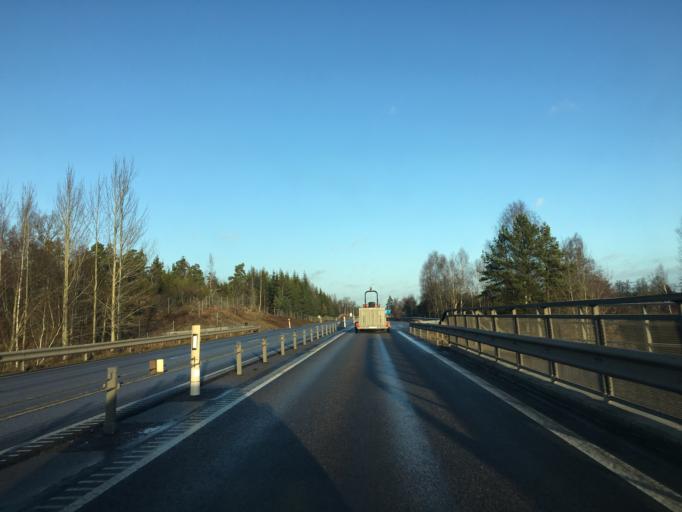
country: SE
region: Kalmar
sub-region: Vasterviks Kommun
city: Vaestervik
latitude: 57.7552
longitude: 16.5571
